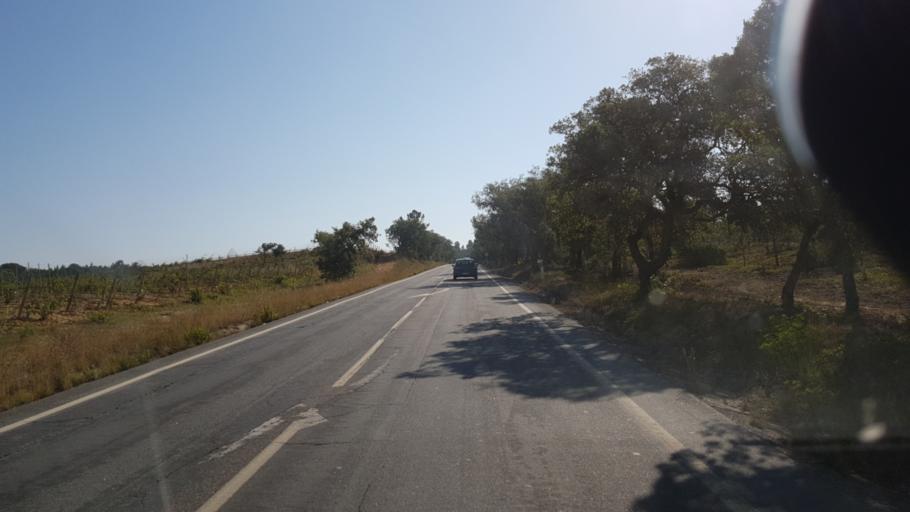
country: PT
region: Setubal
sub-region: Sesimbra
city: Sesimbra
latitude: 38.4820
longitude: -9.0713
